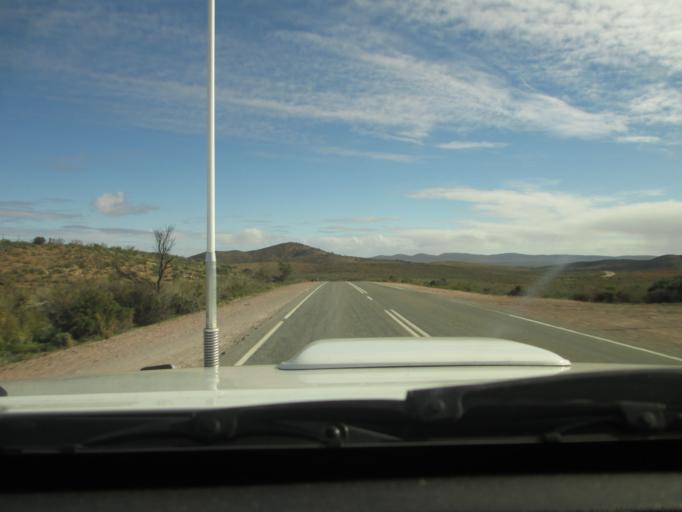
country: AU
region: South Australia
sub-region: Flinders Ranges
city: Quorn
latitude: -31.8084
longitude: 138.3653
